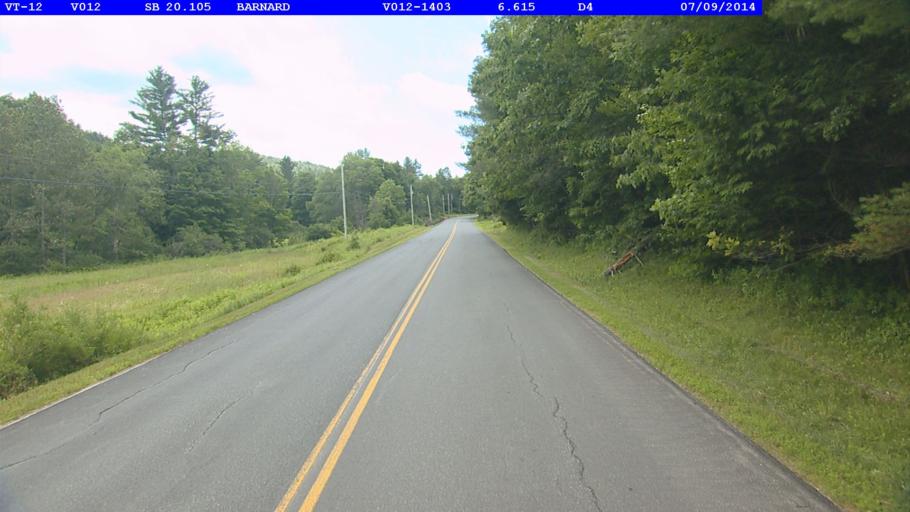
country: US
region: Vermont
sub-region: Windsor County
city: Woodstock
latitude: 43.7521
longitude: -72.6328
